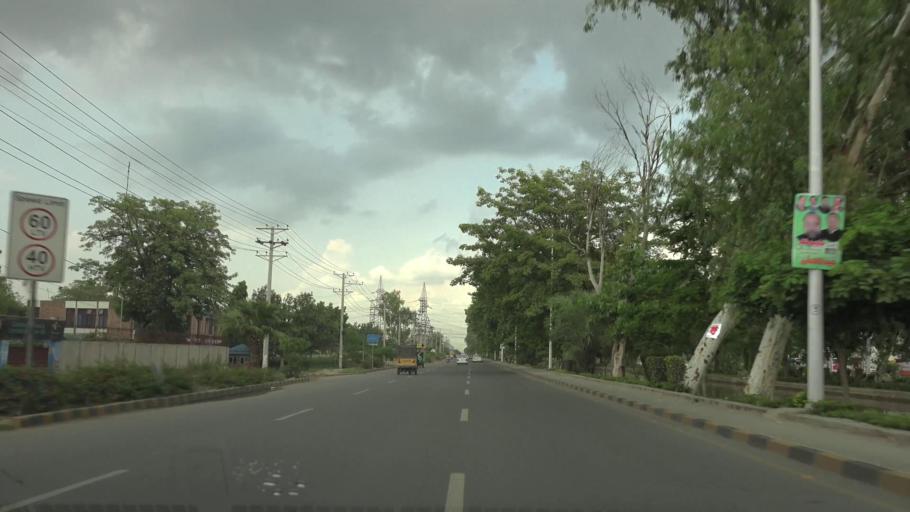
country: PK
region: Punjab
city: Faisalabad
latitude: 31.4305
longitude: 73.1204
